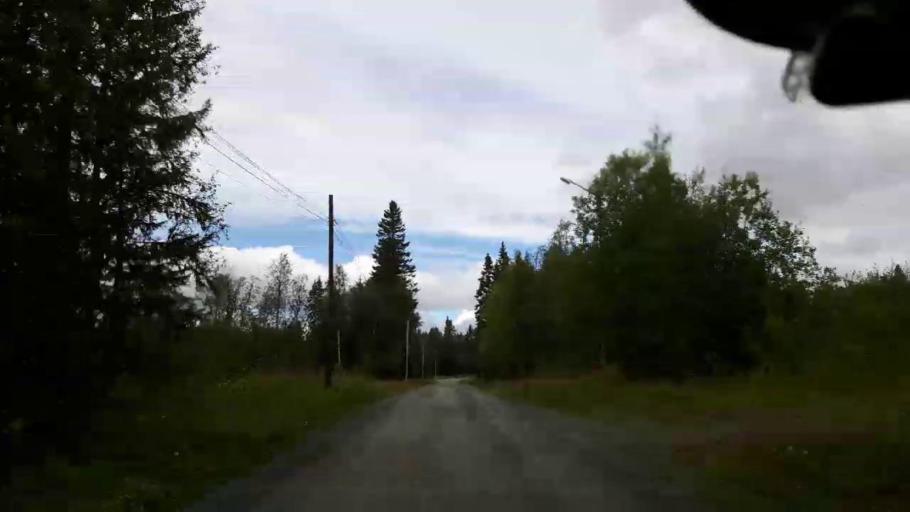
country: SE
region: Jaemtland
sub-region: Krokoms Kommun
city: Valla
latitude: 63.7047
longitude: 13.8713
